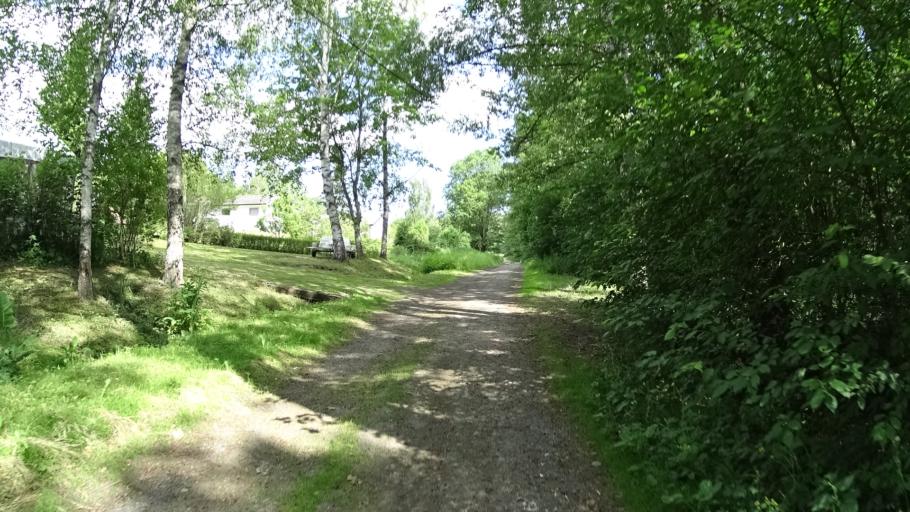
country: FI
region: Uusimaa
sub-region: Raaseporin
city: Pohja
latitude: 60.1038
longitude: 23.5544
